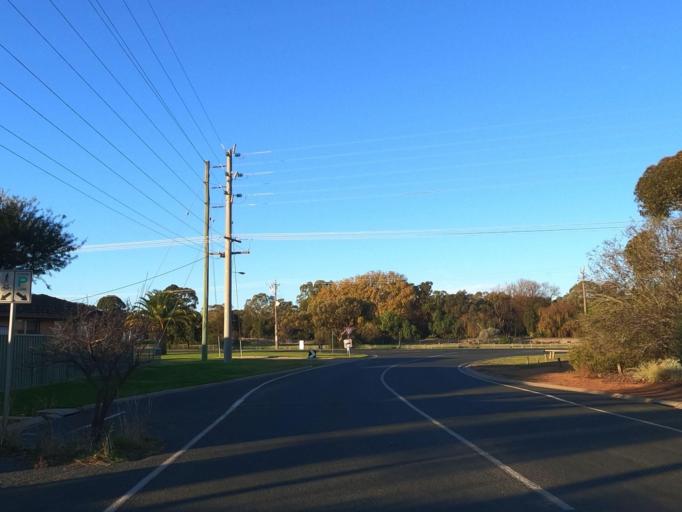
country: AU
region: Victoria
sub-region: Swan Hill
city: Swan Hill
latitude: -35.3588
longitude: 143.5615
